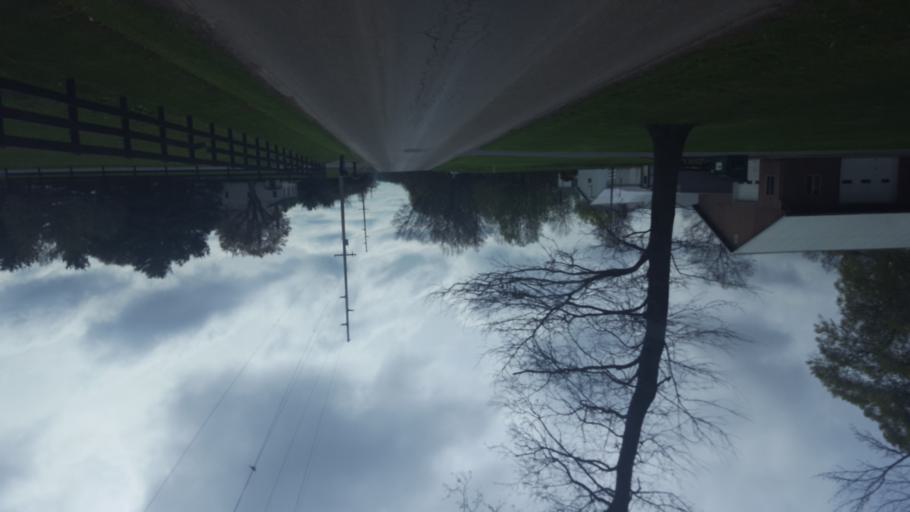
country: US
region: Ohio
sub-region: Wayne County
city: Apple Creek
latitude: 40.7117
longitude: -81.8307
